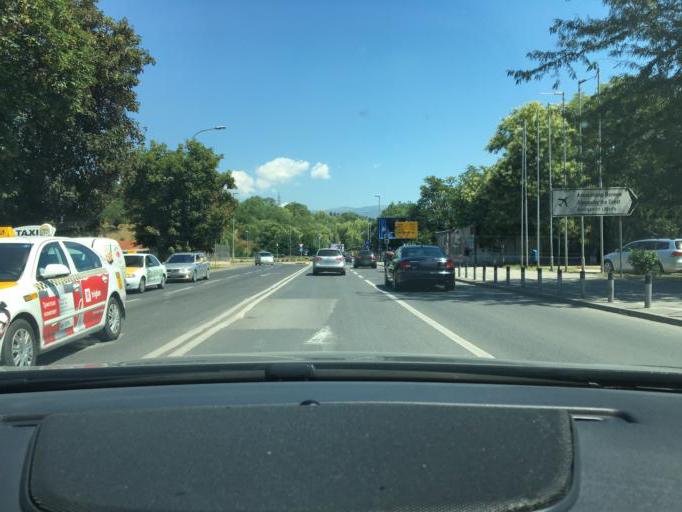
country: MK
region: Karpos
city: Skopje
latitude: 41.9976
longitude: 21.4504
